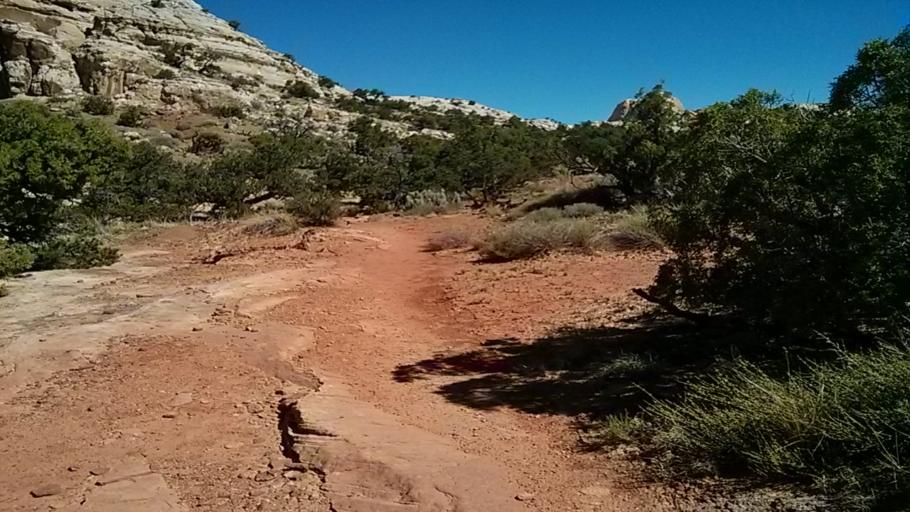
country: US
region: Utah
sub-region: Wayne County
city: Loa
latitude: 38.2942
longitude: -111.2493
